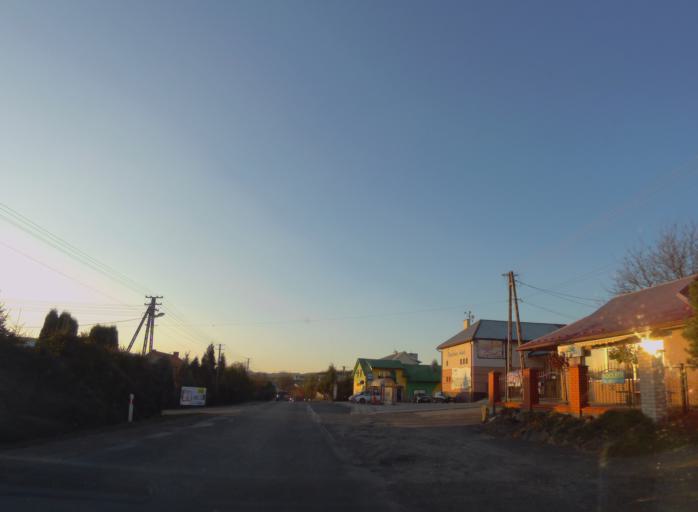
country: PL
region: Subcarpathian Voivodeship
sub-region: Powiat leski
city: Lesko
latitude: 49.4154
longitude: 22.3448
